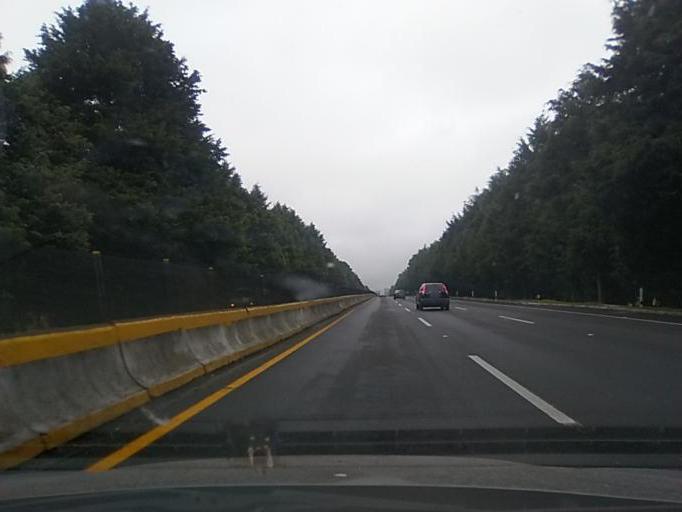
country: MX
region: Mexico City
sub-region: Tlalpan
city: Lomas de Tepemecatl
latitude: 19.1493
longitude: -99.1602
